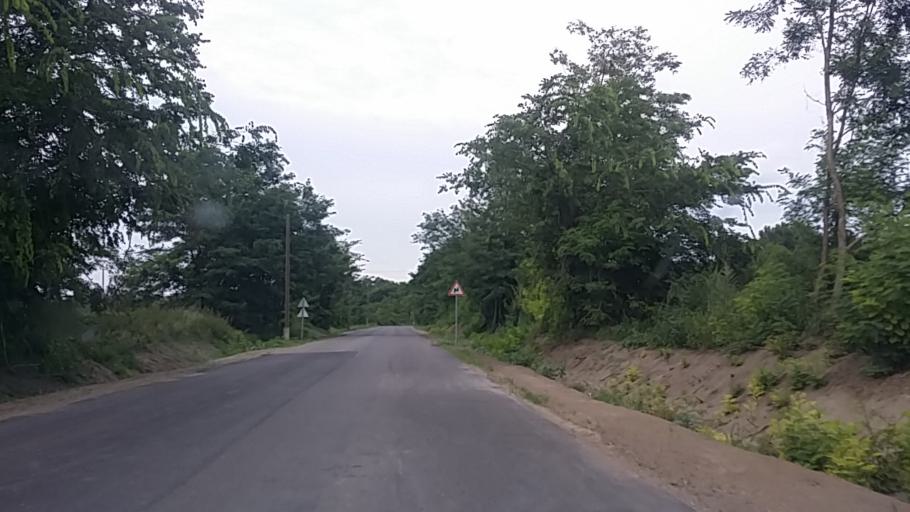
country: HU
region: Tolna
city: Tengelic
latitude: 46.5473
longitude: 18.6989
